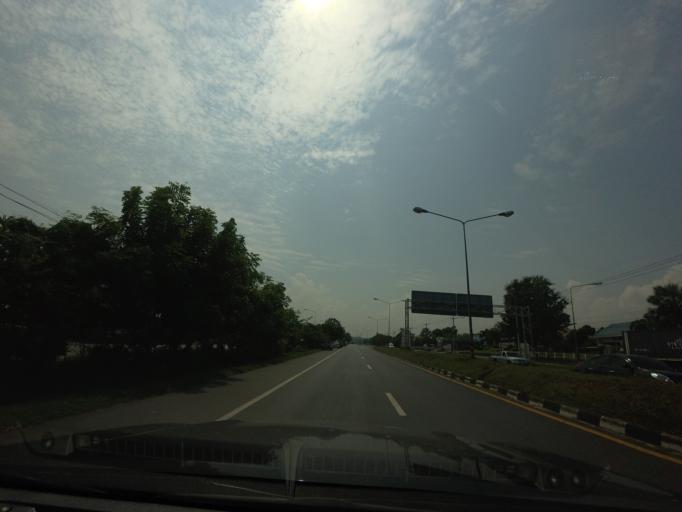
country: TH
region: Phrae
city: Den Chai
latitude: 17.9663
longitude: 100.0662
